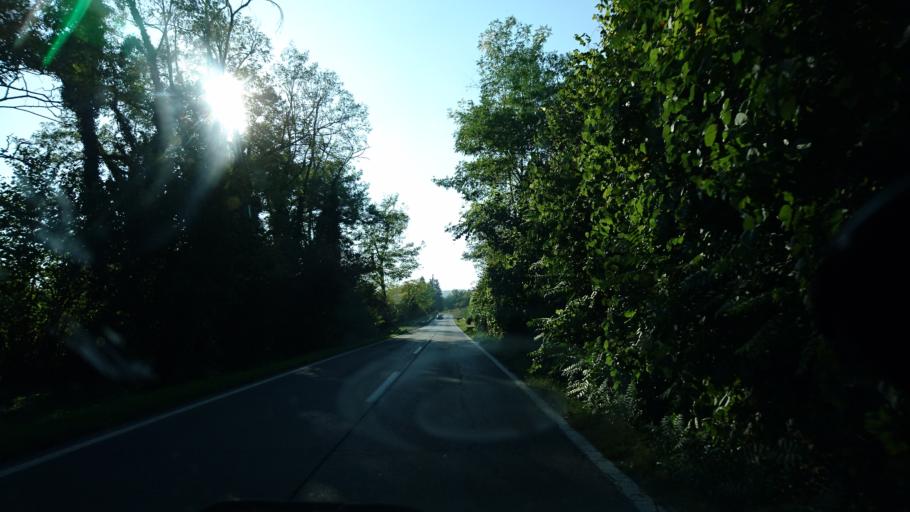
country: IT
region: Piedmont
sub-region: Provincia di Alessandria
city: Bistagno
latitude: 44.6608
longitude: 8.3550
